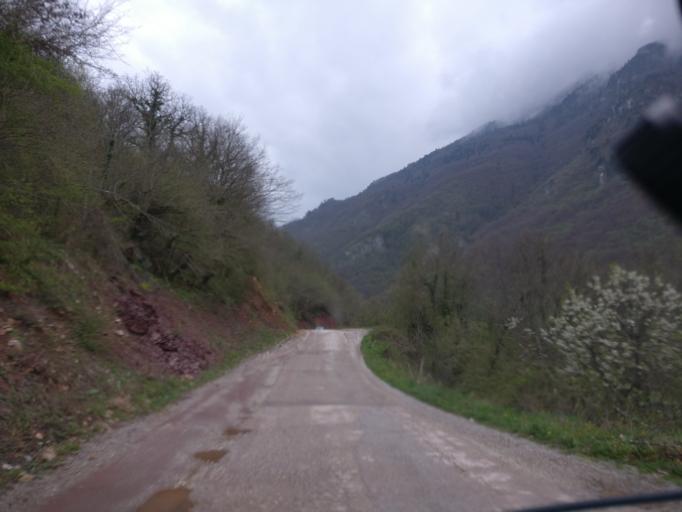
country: BA
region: Republika Srpska
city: Foca
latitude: 43.3572
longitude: 18.8164
